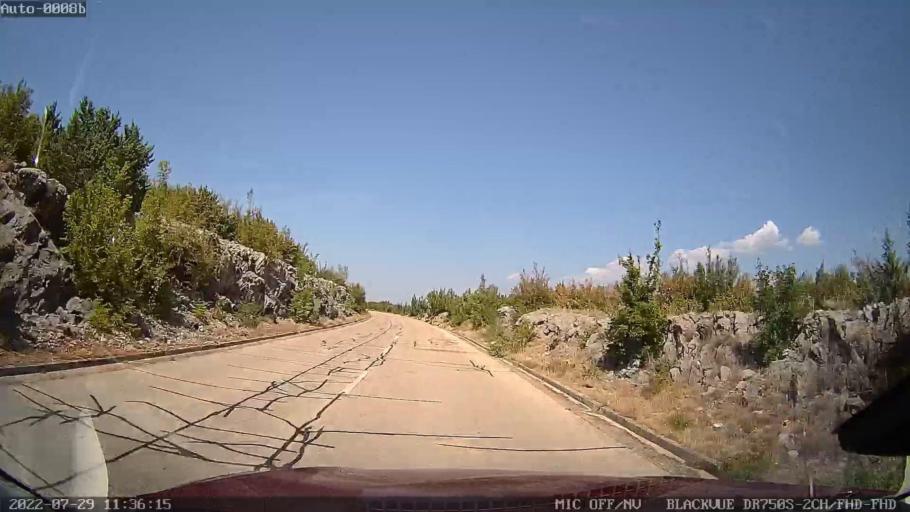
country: HR
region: Zadarska
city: Obrovac
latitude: 44.1884
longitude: 15.7012
